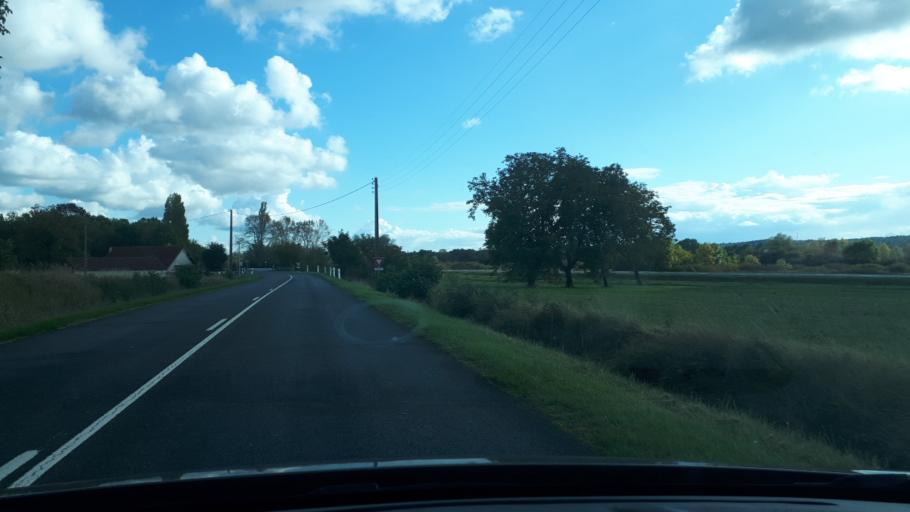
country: FR
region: Centre
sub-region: Departement du Loir-et-Cher
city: Mareuil-sur-Cher
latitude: 47.3109
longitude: 1.3368
